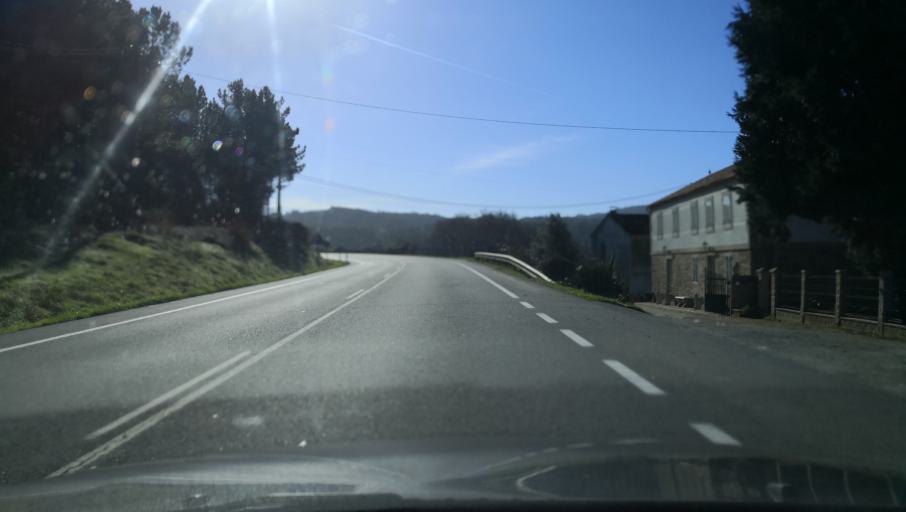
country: ES
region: Galicia
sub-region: Provincia da Coruna
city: Ribeira
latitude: 42.7536
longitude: -8.3538
